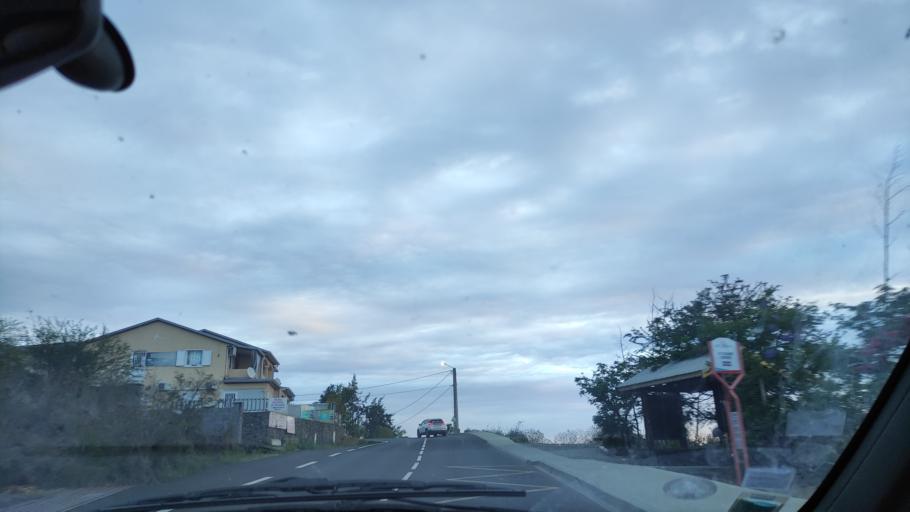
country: RE
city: Piton Saint-Leu
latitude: -21.2077
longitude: 55.2972
